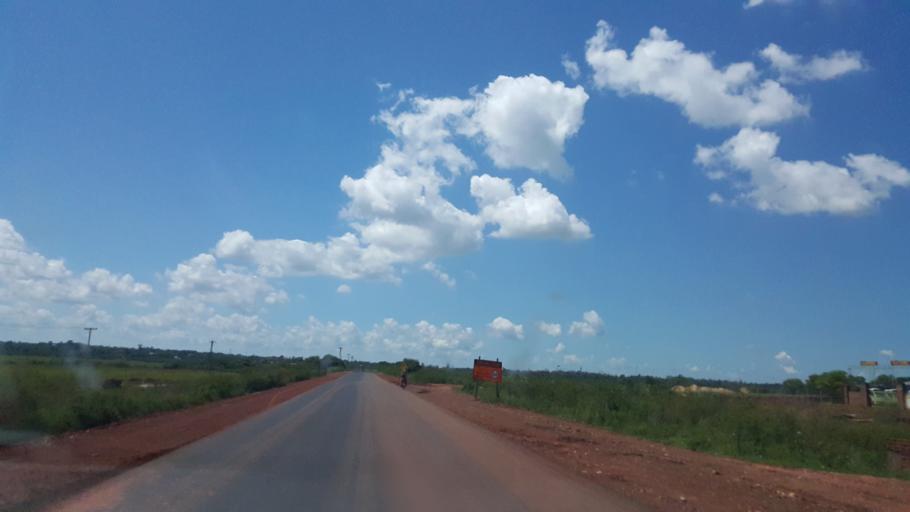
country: AR
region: Corrientes
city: Santo Tome
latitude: -28.5259
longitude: -56.0549
